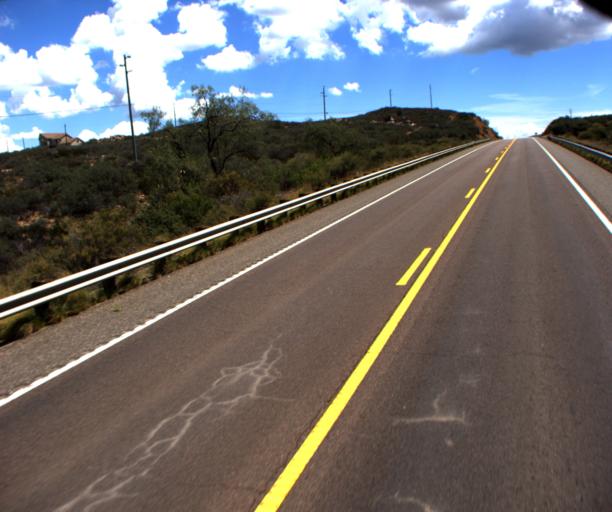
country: US
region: Arizona
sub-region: Yavapai County
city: Dewey-Humboldt
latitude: 34.5429
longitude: -112.1886
